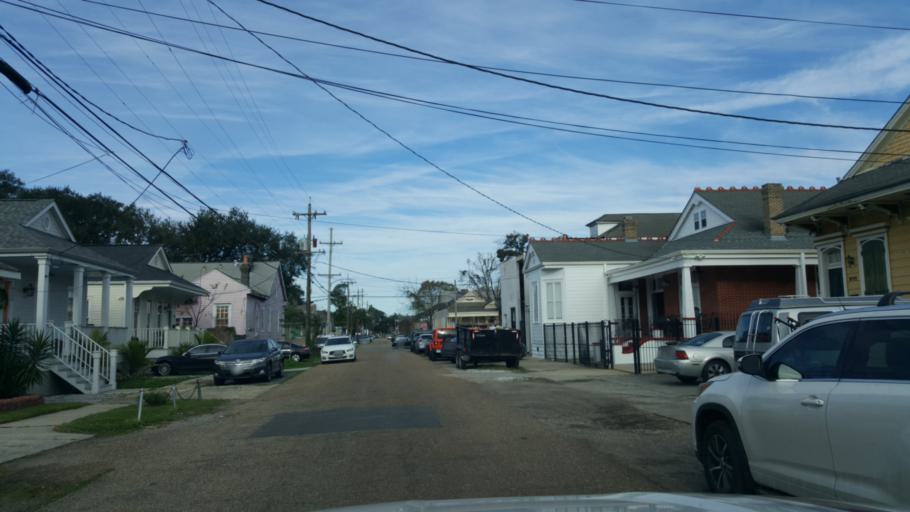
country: US
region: Louisiana
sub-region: Orleans Parish
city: New Orleans
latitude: 29.9742
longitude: -90.0717
